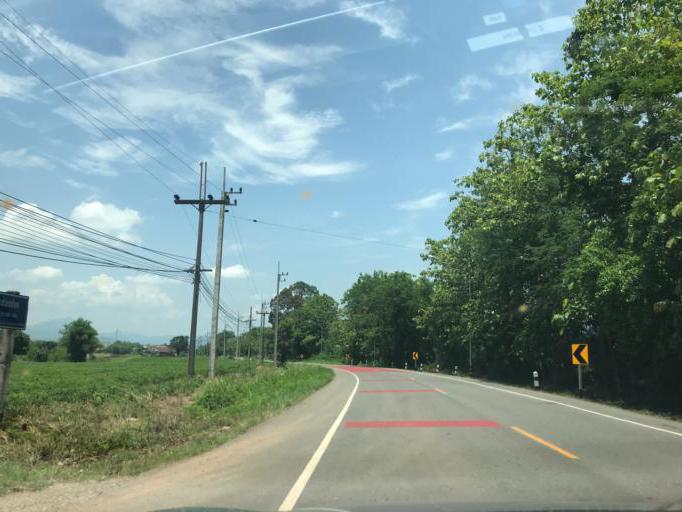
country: TH
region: Phayao
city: Phu Sang
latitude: 19.5812
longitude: 100.3048
